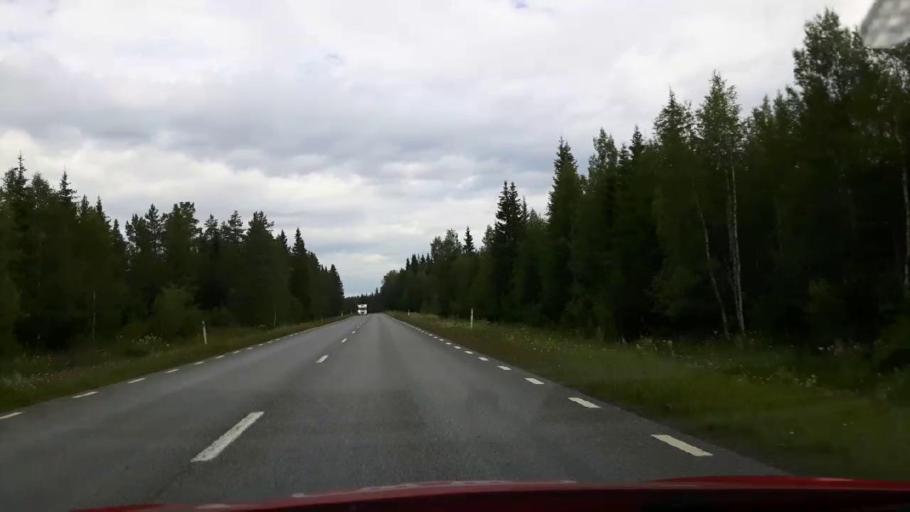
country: SE
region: Jaemtland
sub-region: Stroemsunds Kommun
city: Stroemsund
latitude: 63.5512
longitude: 15.3727
